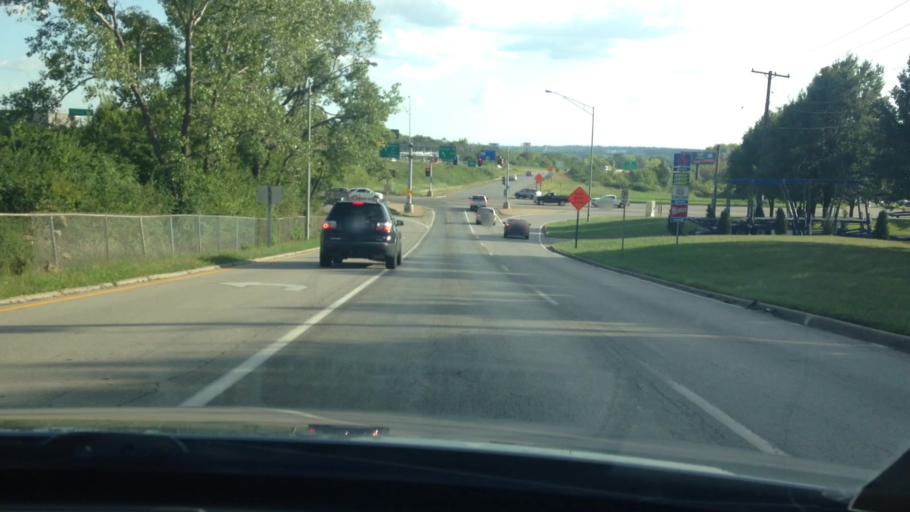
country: US
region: Missouri
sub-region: Clay County
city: Claycomo
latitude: 39.1696
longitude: -94.4938
